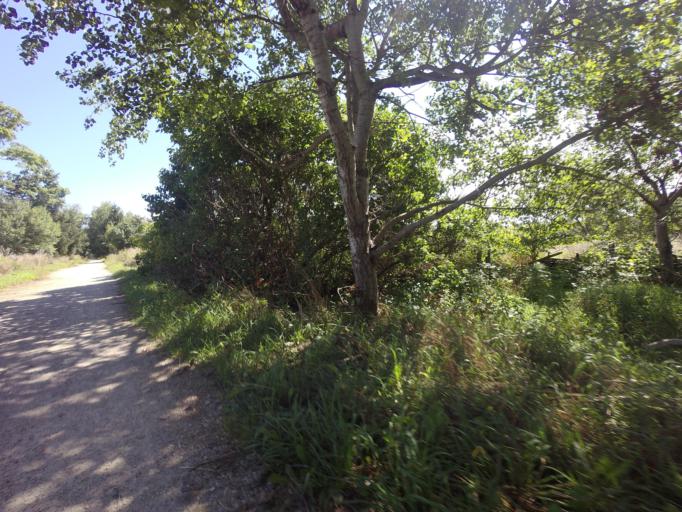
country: CA
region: Ontario
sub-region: Wellington County
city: Guelph
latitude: 43.6962
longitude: -80.4081
